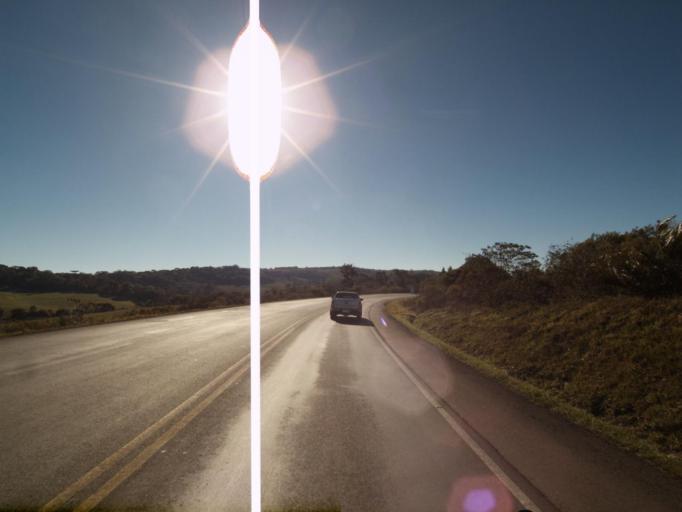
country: BR
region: Santa Catarina
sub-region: Concordia
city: Concordia
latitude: -26.9073
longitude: -51.9112
